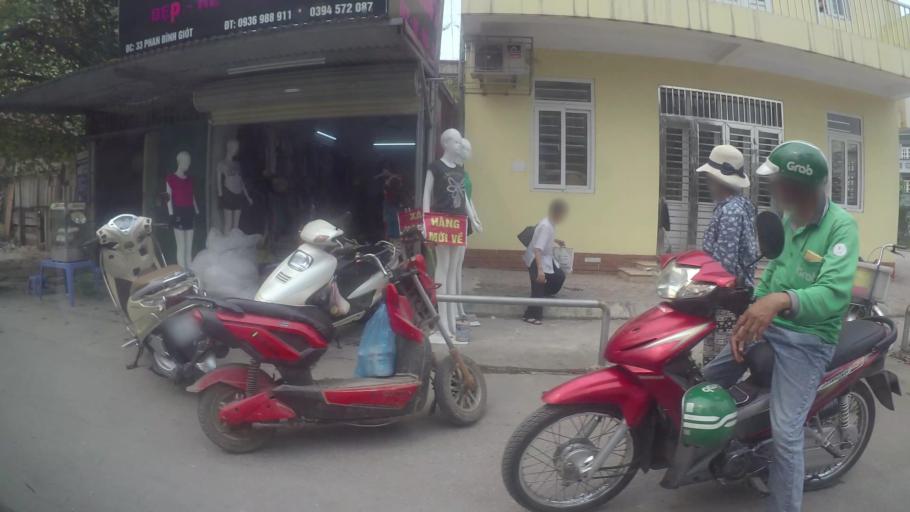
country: VN
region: Ha Noi
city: Ha Dong
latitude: 20.9663
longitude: 105.7656
